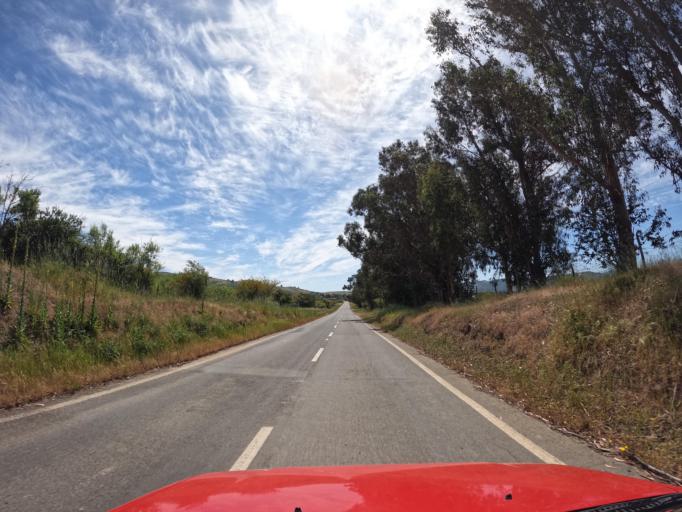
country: CL
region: Maule
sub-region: Provincia de Talca
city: Talca
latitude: -35.0376
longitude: -71.7563
